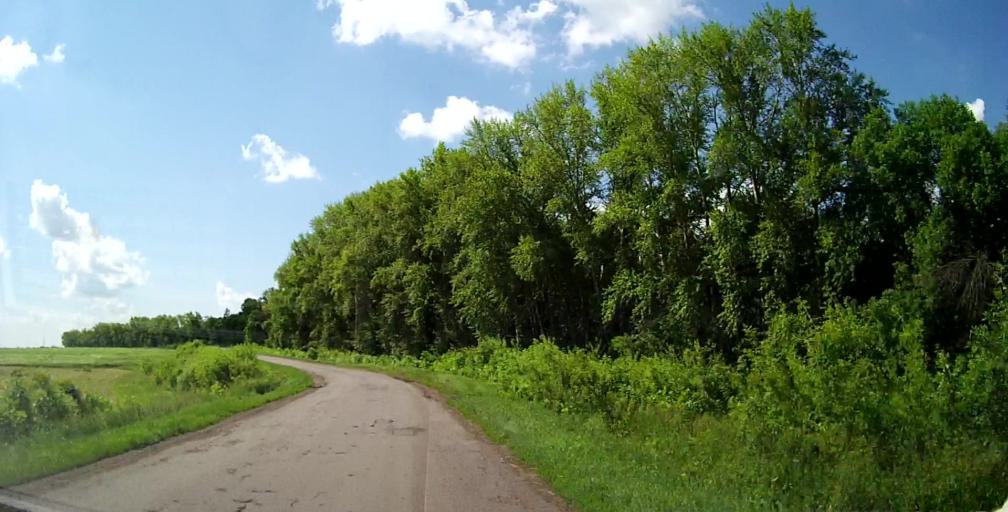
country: RU
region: Lipetsk
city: Chaplygin
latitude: 53.3035
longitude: 39.9519
